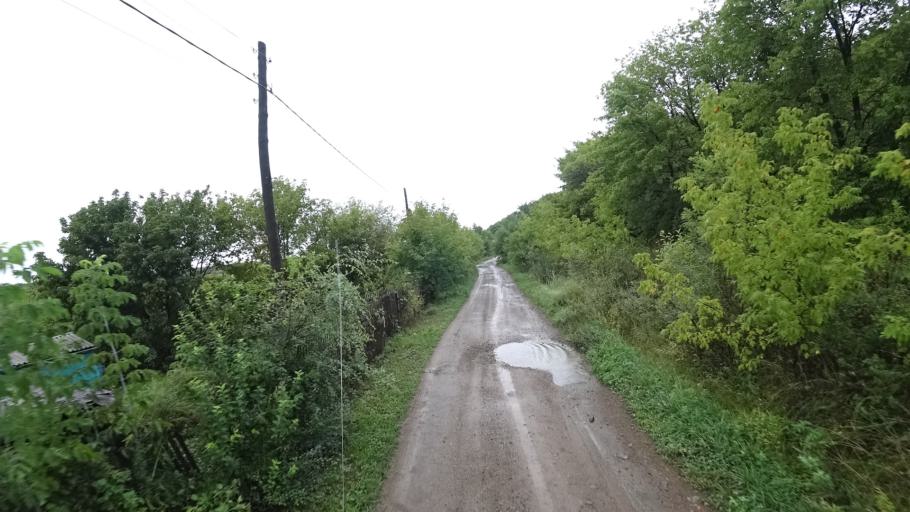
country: RU
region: Primorskiy
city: Monastyrishche
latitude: 44.2650
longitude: 132.4042
